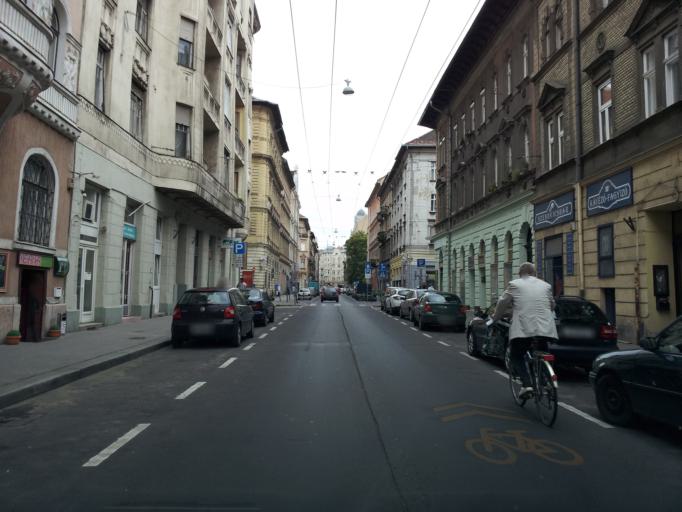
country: HU
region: Budapest
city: Budapest VII. keruelet
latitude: 47.5048
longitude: 19.0817
